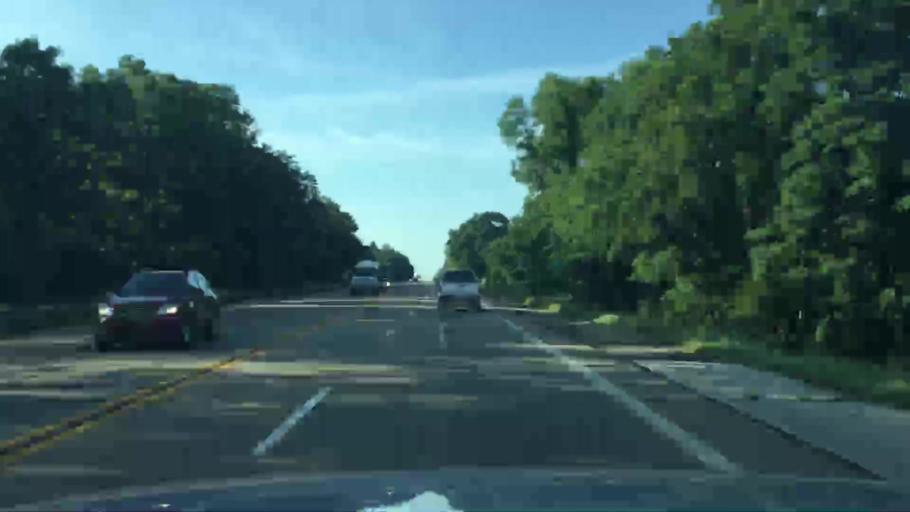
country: US
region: Michigan
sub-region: Jackson County
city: Vandercook Lake
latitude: 42.0912
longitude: -84.3638
